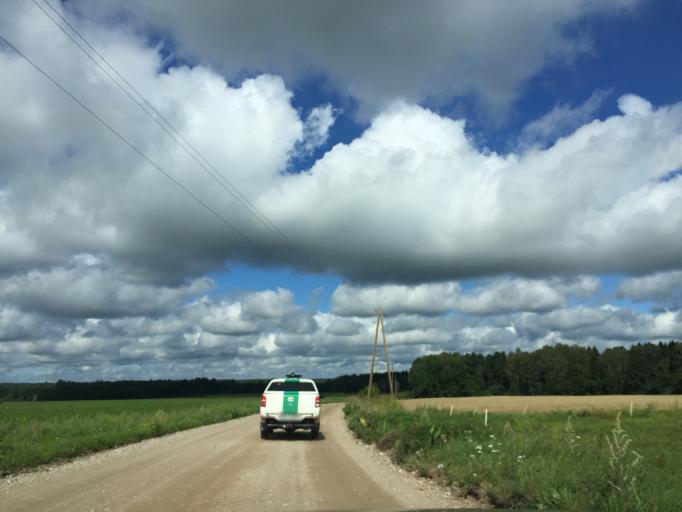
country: LV
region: Ligatne
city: Ligatne
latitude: 57.2110
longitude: 24.9577
